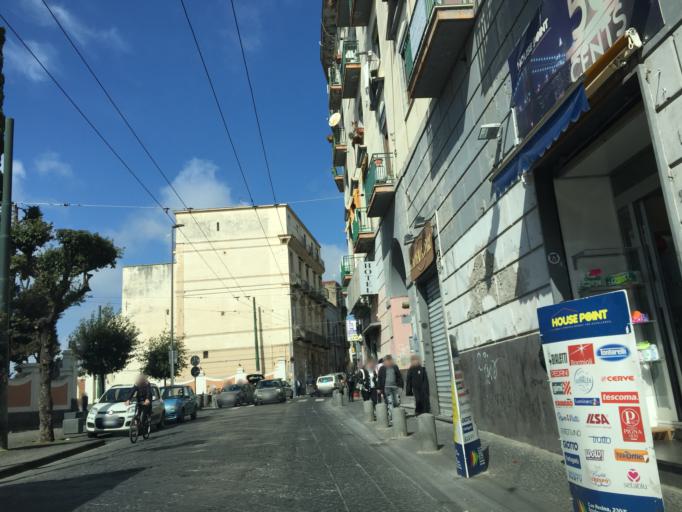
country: IT
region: Campania
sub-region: Provincia di Napoli
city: Portici
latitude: 40.8057
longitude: 14.3496
